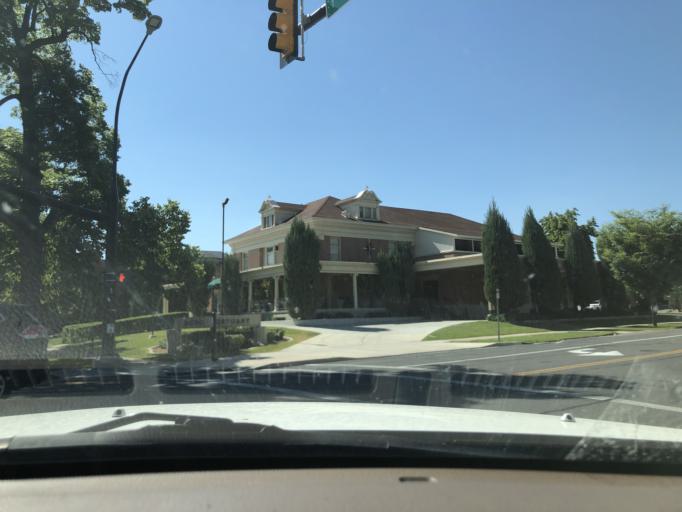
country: US
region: Utah
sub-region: Utah County
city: Provo
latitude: 40.2338
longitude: -111.6550
